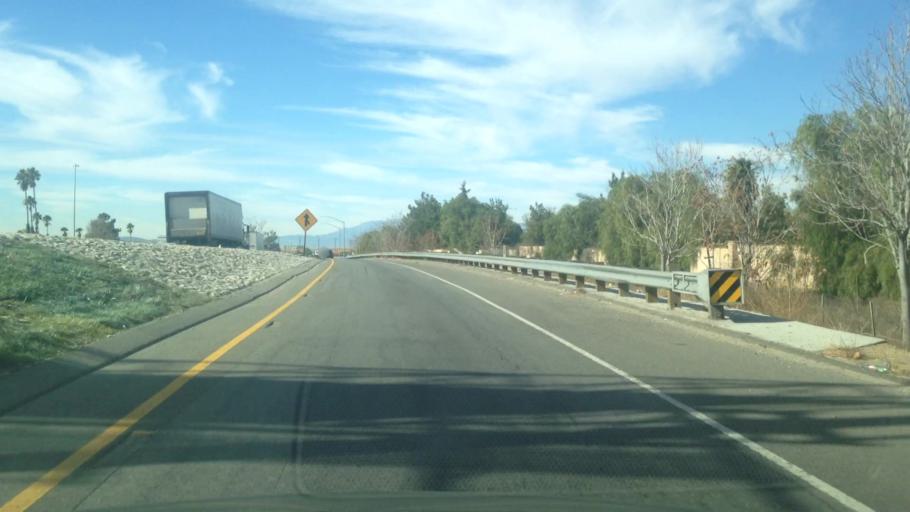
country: US
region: California
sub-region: Riverside County
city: Beaumont
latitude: 33.9327
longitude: -116.9876
